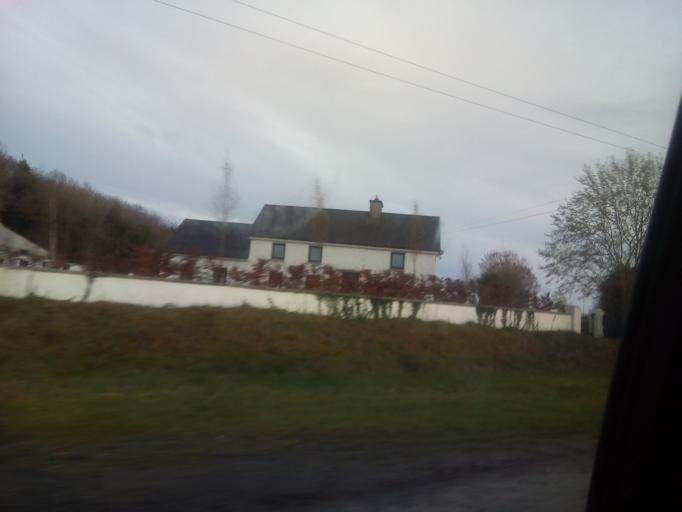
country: IE
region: Leinster
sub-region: Laois
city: Abbeyleix
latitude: 52.8561
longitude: -7.3856
